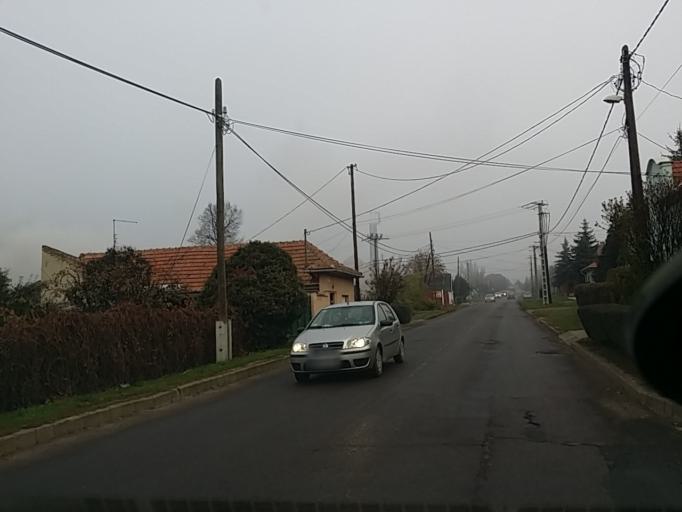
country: HU
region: Heves
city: Gyongyos
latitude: 47.7957
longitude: 19.9302
